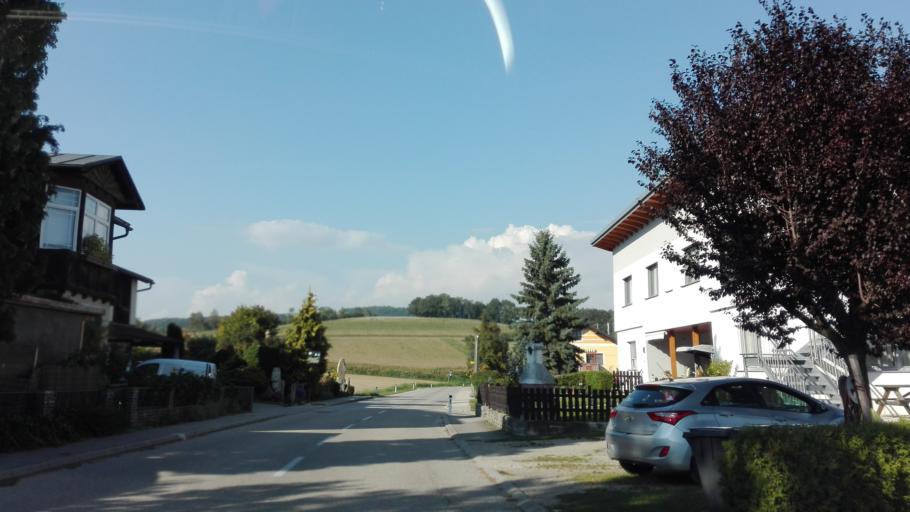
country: AT
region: Upper Austria
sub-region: Politischer Bezirk Perg
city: Perg
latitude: 48.2888
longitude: 14.5922
